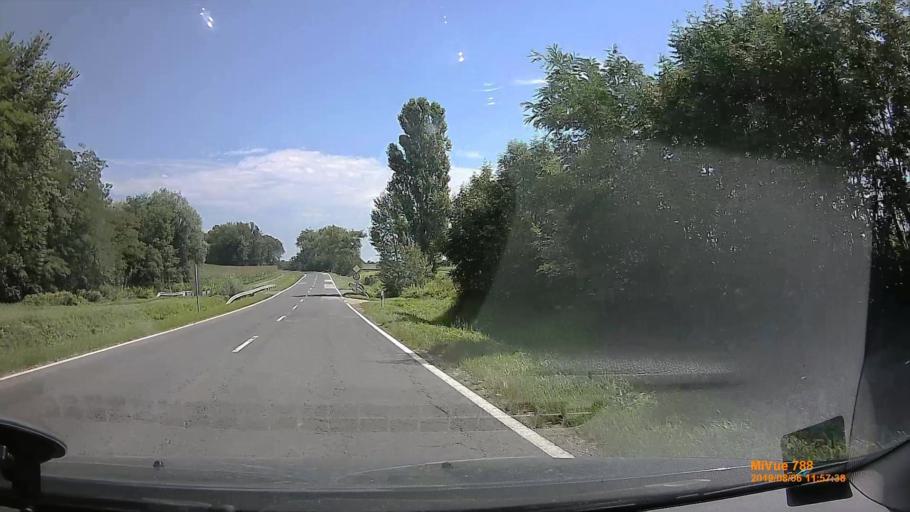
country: HU
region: Zala
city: Becsehely
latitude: 46.4396
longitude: 16.7583
